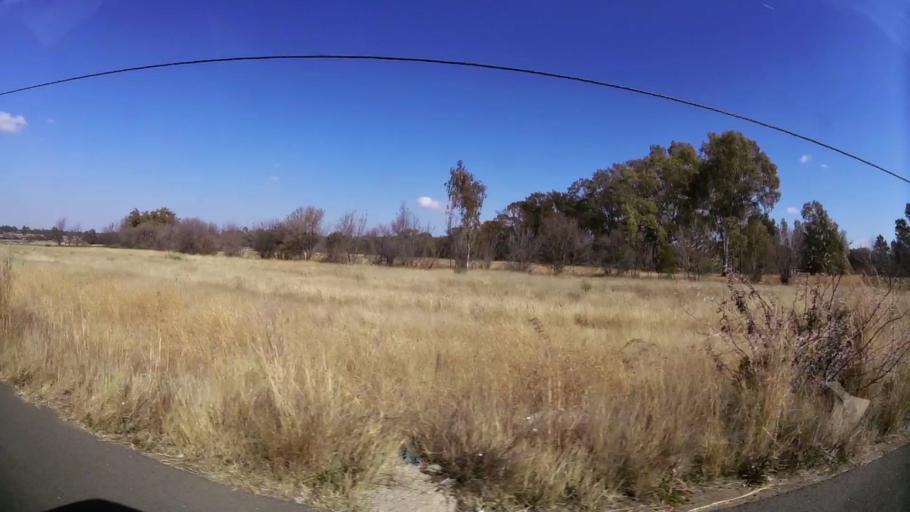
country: ZA
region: Orange Free State
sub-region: Mangaung Metropolitan Municipality
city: Bloemfontein
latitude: -29.1172
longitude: 26.2651
